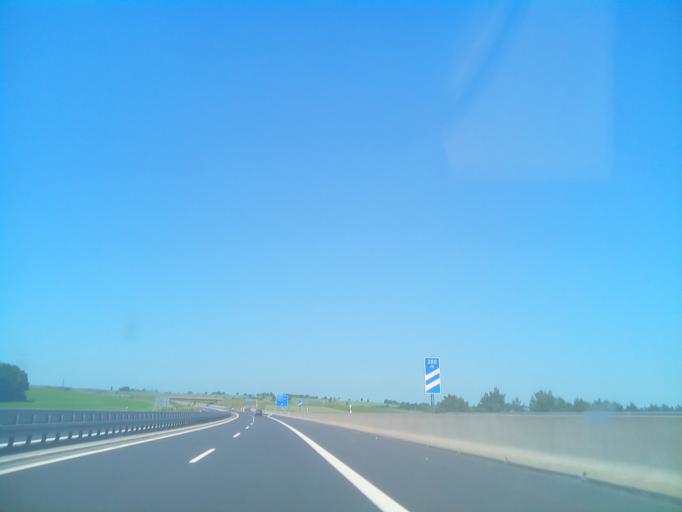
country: DE
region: Bavaria
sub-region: Regierungsbezirk Unterfranken
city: Rannungen
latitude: 50.1950
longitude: 10.2122
